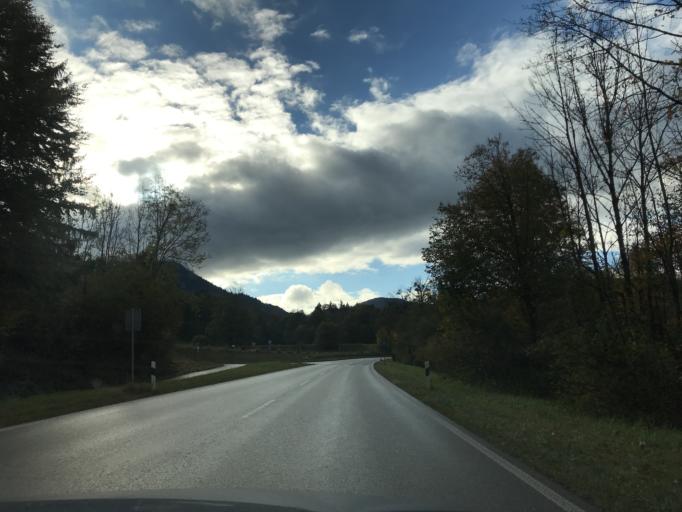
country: DE
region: Bavaria
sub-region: Upper Bavaria
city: Lenggries
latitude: 47.6586
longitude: 11.5869
